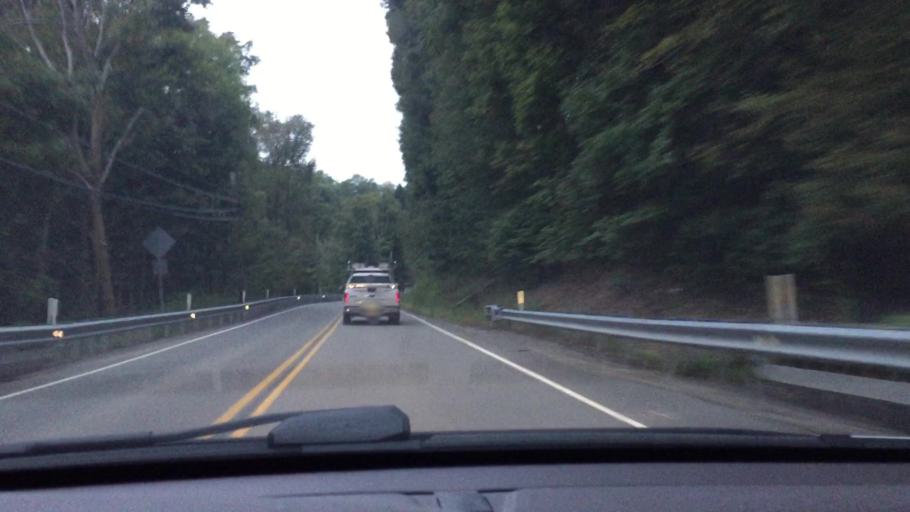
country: US
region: Pennsylvania
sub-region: Westmoreland County
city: West Newton
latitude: 40.2021
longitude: -79.7905
